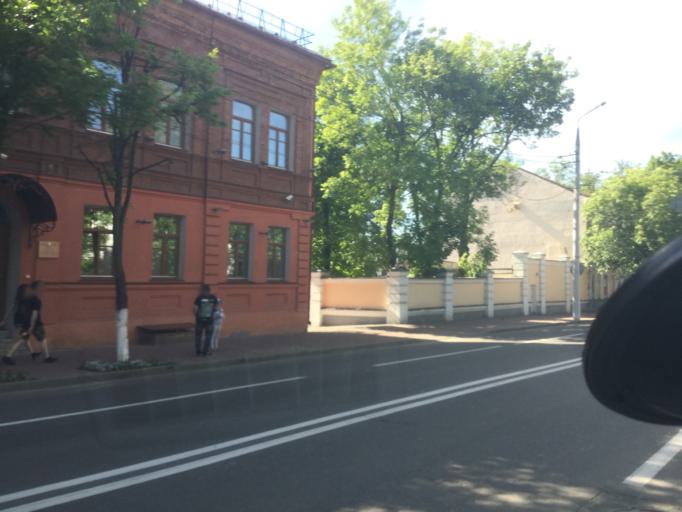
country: BY
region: Vitebsk
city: Vitebsk
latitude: 55.1885
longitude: 30.2011
